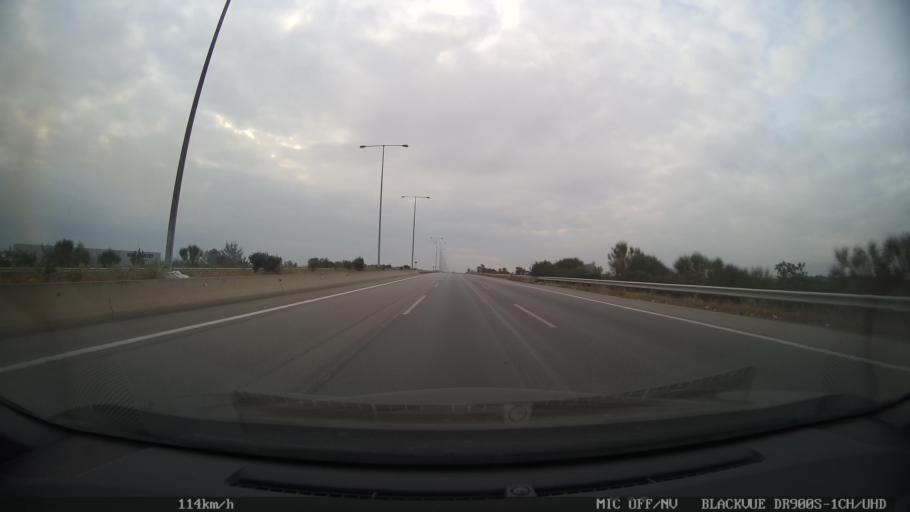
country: GR
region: Central Macedonia
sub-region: Nomos Thessalonikis
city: Nea Magnisia
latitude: 40.6702
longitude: 22.8338
